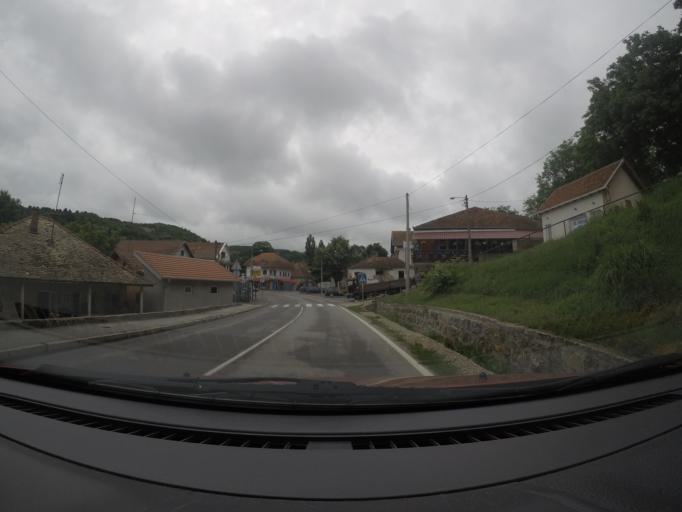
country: RS
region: Central Serbia
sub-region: Belgrade
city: Sopot
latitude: 44.5741
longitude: 20.5588
